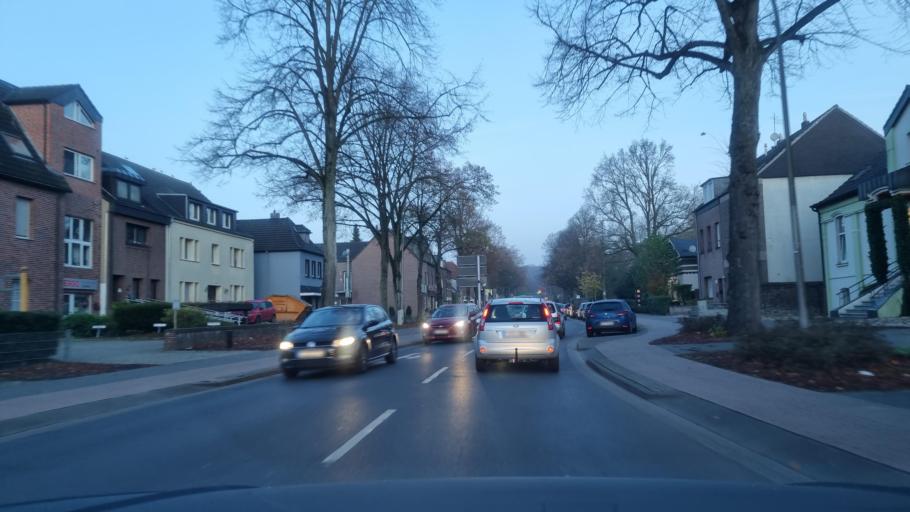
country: DE
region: North Rhine-Westphalia
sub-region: Regierungsbezirk Dusseldorf
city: Kleve
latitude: 51.7833
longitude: 6.1296
